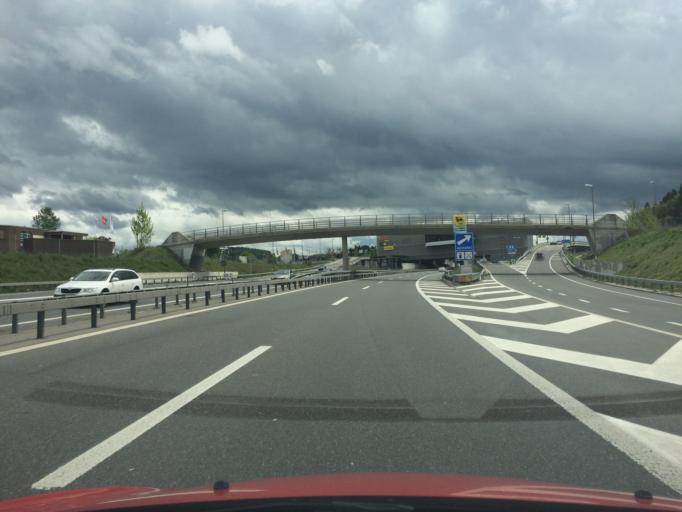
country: CH
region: Zurich
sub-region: Bezirk Affoltern
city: Obfelden / Toussen
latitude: 47.2738
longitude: 8.4365
